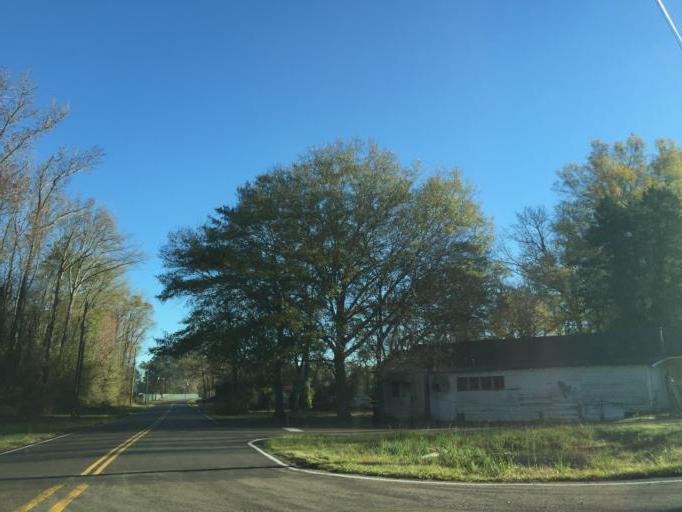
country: US
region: Mississippi
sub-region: Hinds County
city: Jackson
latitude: 32.2826
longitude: -90.1632
